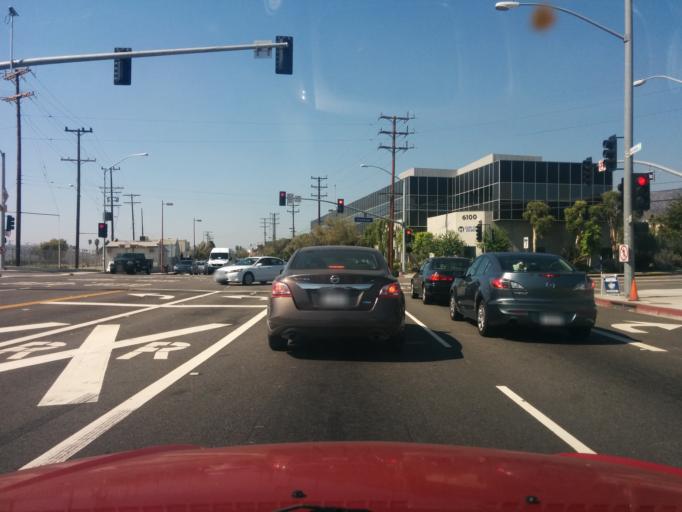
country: US
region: California
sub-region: Los Angeles County
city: North Glendale
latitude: 34.1614
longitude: -118.2822
